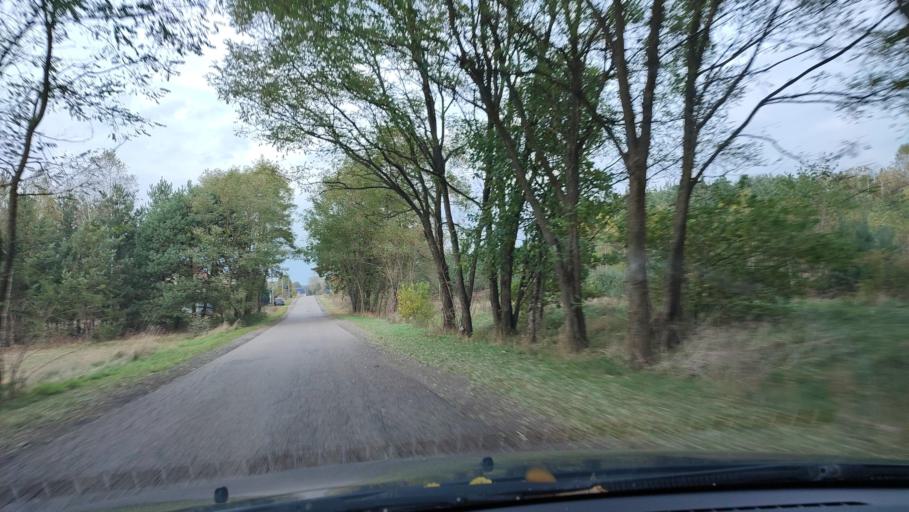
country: PL
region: Masovian Voivodeship
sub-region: Powiat mlawski
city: Mlawa
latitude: 53.1642
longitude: 20.3632
